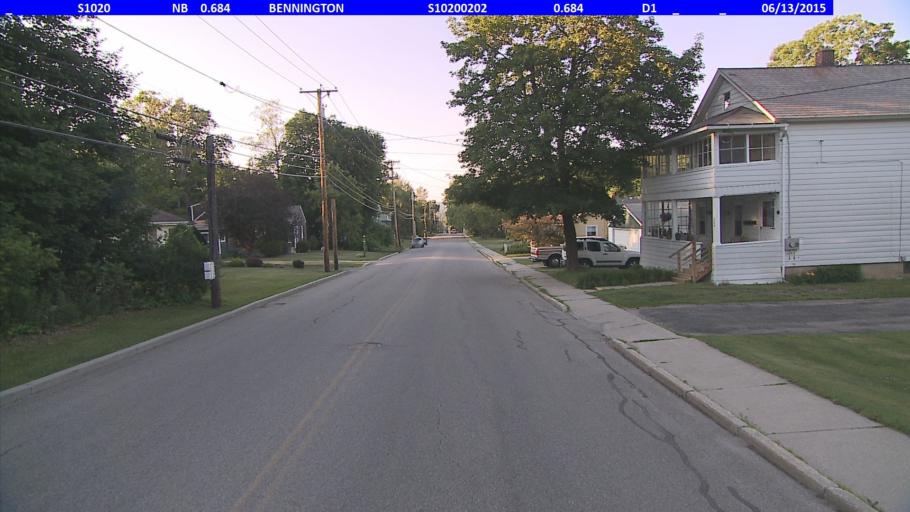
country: US
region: Vermont
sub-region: Bennington County
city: Bennington
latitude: 42.8749
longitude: -73.2039
